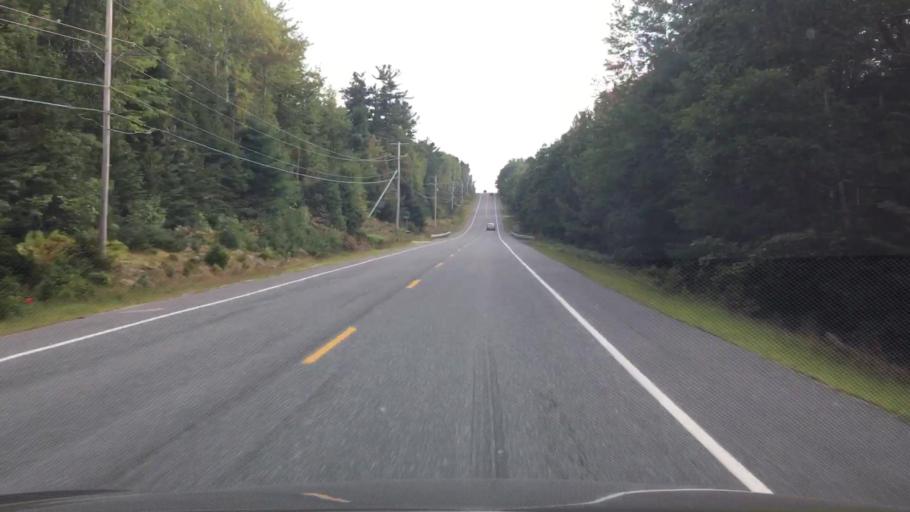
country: US
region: Maine
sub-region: Hancock County
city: Surry
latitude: 44.4838
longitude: -68.5151
